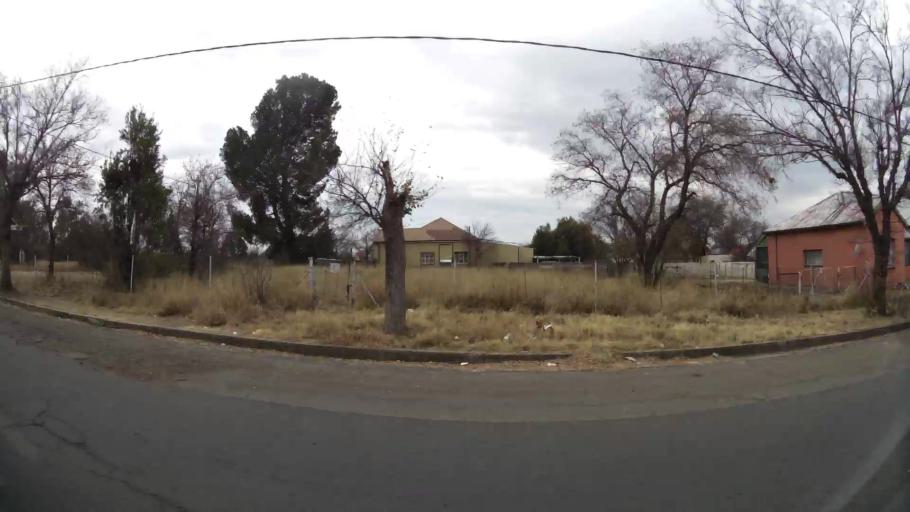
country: ZA
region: Orange Free State
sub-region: Fezile Dabi District Municipality
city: Kroonstad
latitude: -27.6546
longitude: 27.2419
